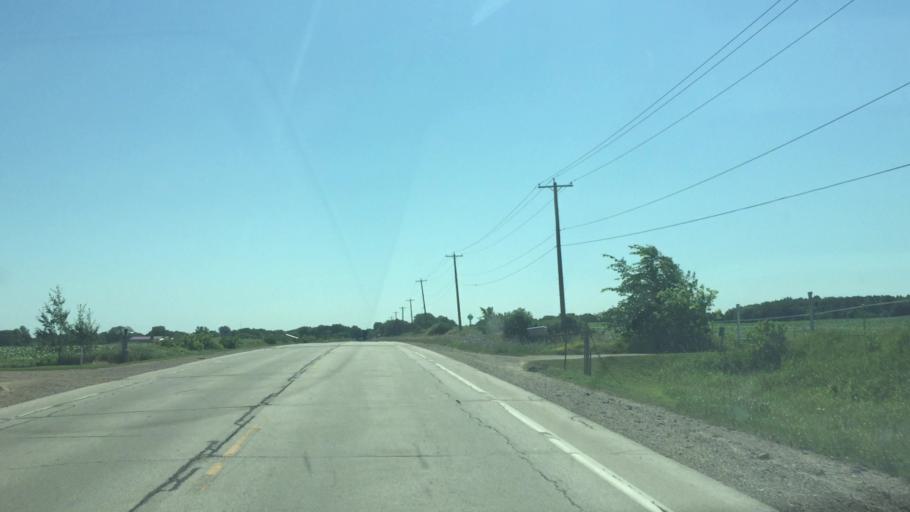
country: US
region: Wisconsin
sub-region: Calumet County
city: Hilbert
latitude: 44.1402
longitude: -88.1837
